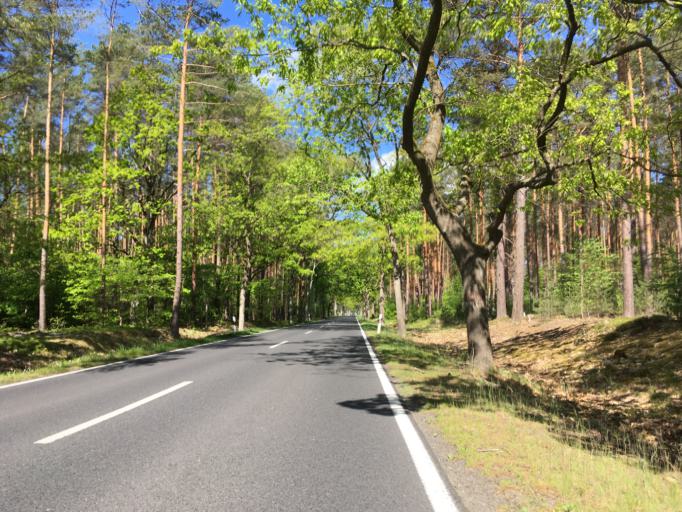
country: DE
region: Brandenburg
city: Birkenwerder
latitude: 52.7207
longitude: 13.3318
